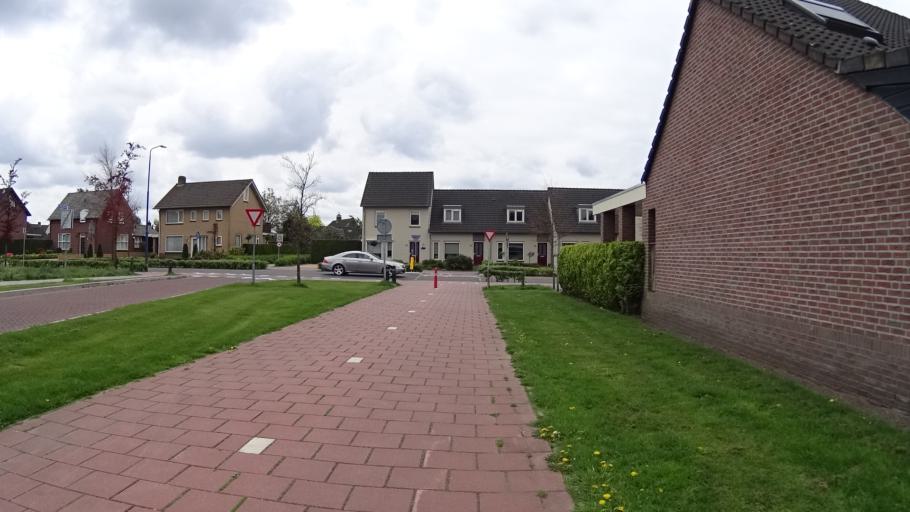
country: NL
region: North Brabant
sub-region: Gemeente Boekel
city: Boekel
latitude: 51.6026
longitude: 5.6827
